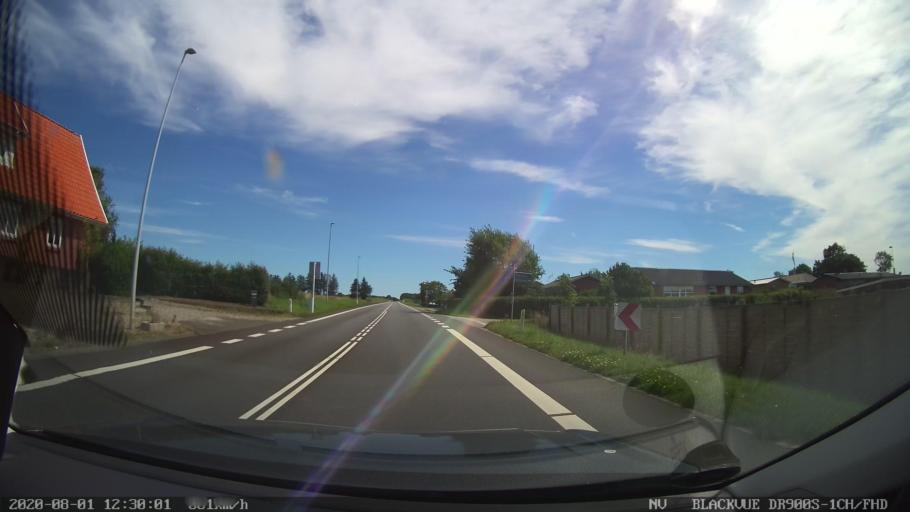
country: DK
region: Central Jutland
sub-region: Viborg Kommune
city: Stoholm
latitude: 56.4355
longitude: 9.1352
